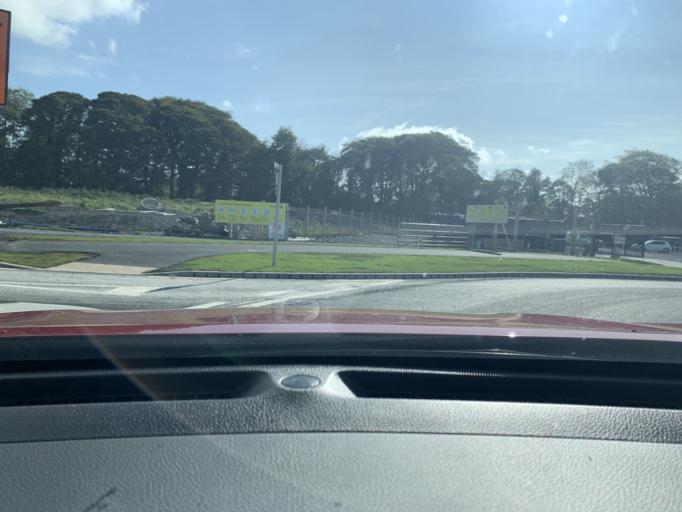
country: IE
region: Connaught
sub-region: Sligo
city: Collooney
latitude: 54.1762
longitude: -8.4810
